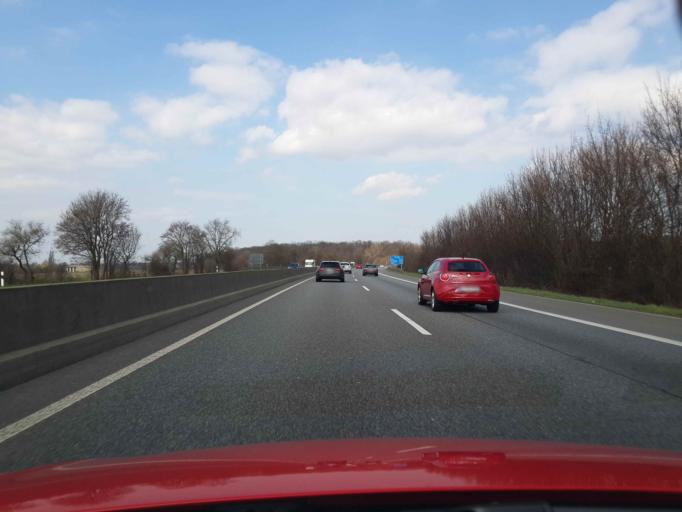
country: DE
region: Hesse
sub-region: Regierungsbezirk Darmstadt
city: Gross-Gerau
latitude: 49.9338
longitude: 8.4842
